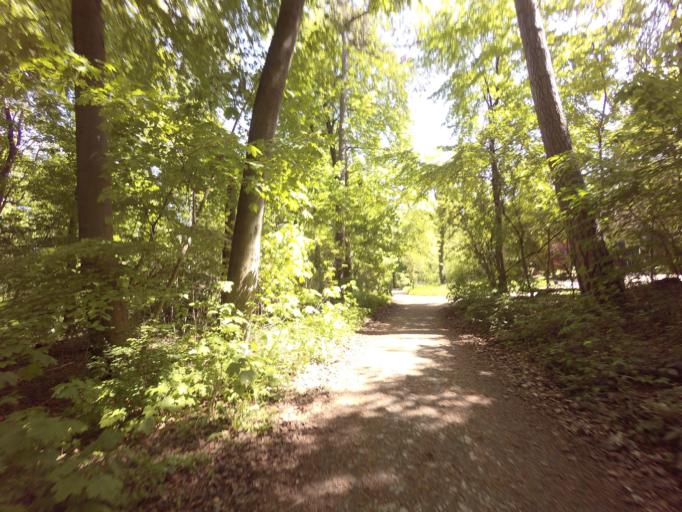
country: DE
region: Lower Saxony
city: Hildesheim
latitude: 52.1362
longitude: 9.9944
